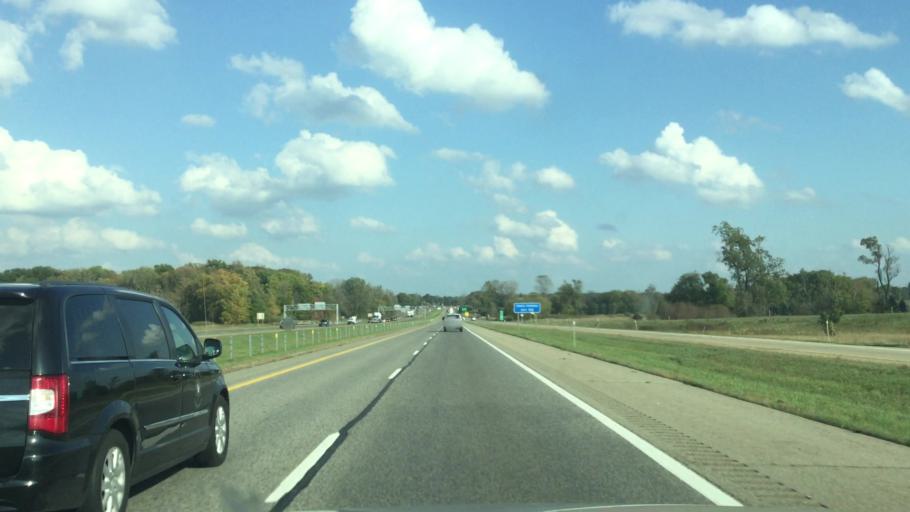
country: US
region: Michigan
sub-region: Calhoun County
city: Marshall
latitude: 42.2972
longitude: -84.9951
